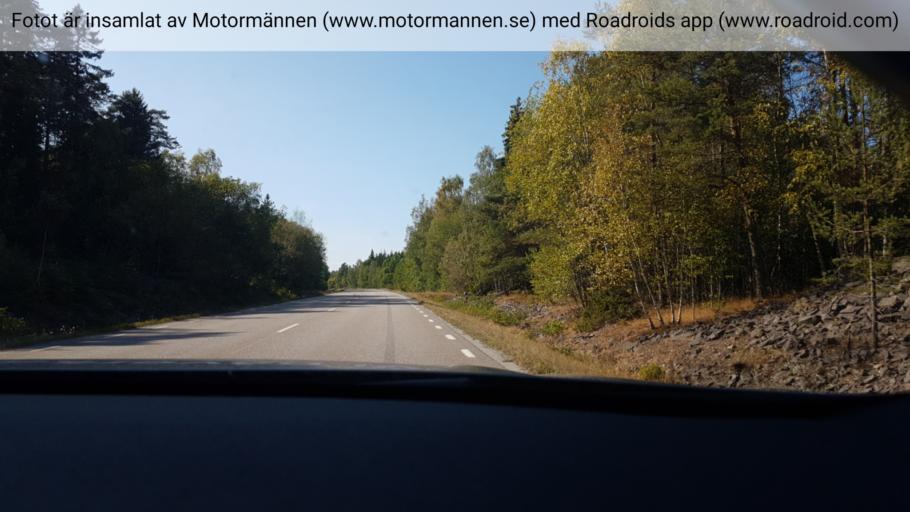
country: SE
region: Vaestra Goetaland
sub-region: Gotene Kommun
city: Goetene
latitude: 58.6213
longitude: 13.4794
